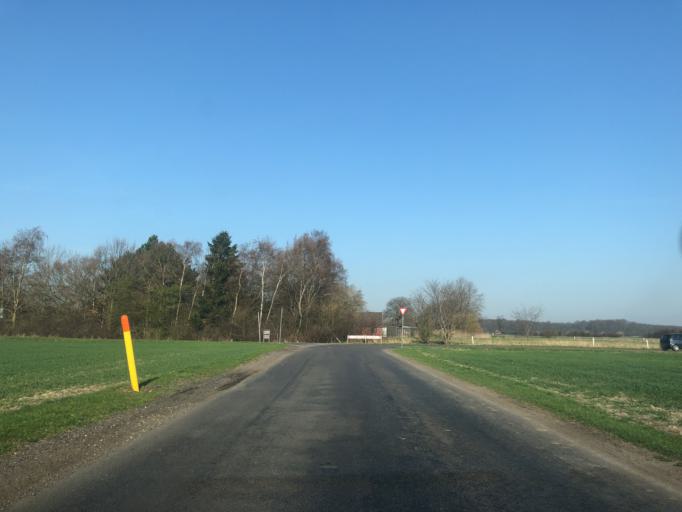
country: DK
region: Zealand
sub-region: Stevns Kommune
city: Store Heddinge
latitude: 55.2809
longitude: 12.3152
